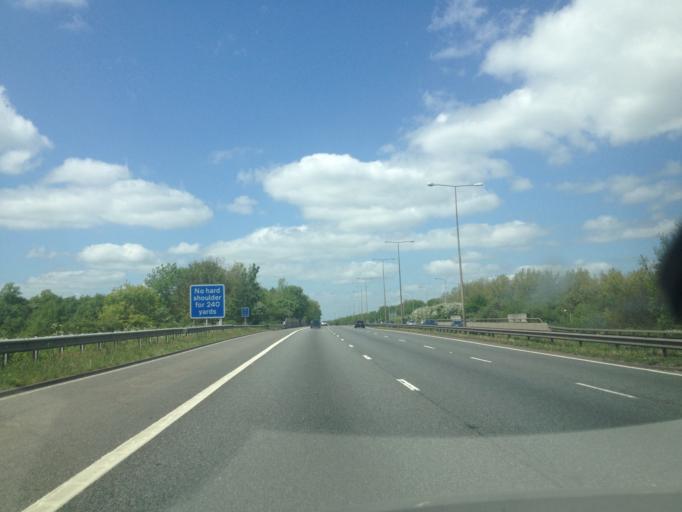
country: GB
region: England
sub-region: Hertfordshire
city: Elstree
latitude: 51.6416
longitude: -0.3207
